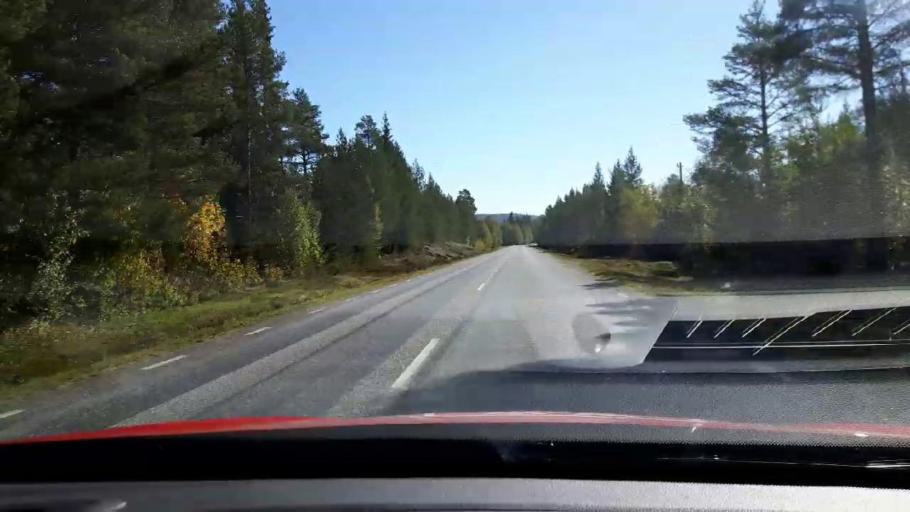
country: SE
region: Jaemtland
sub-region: Harjedalens Kommun
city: Sveg
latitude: 62.3542
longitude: 14.0218
